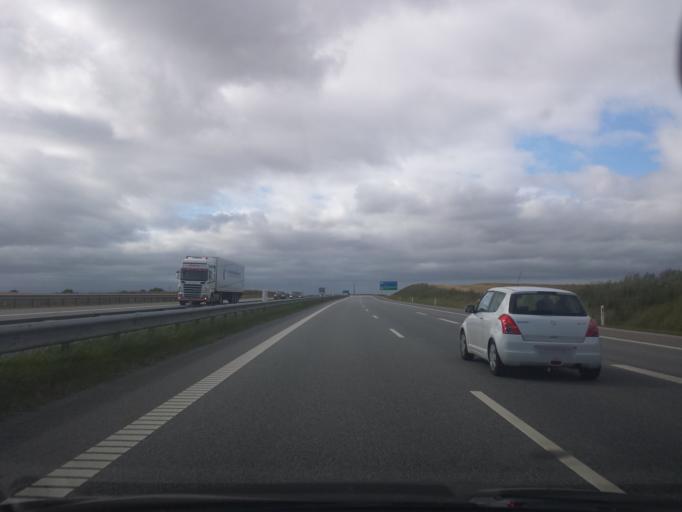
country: DK
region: South Denmark
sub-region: Sonderborg Kommune
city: Dybbol
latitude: 54.9265
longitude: 9.7180
